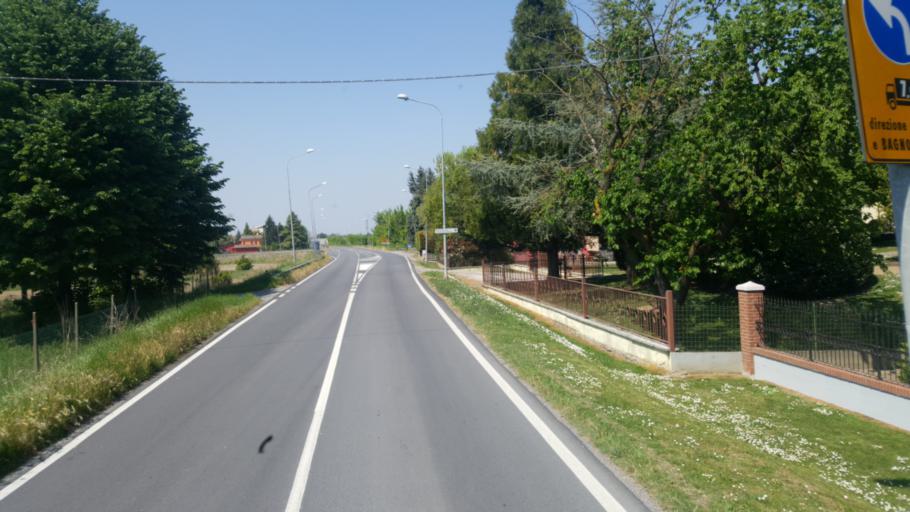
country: IT
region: Lombardy
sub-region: Provincia di Mantova
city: San Benedetto Po
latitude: 45.0302
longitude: 10.9407
